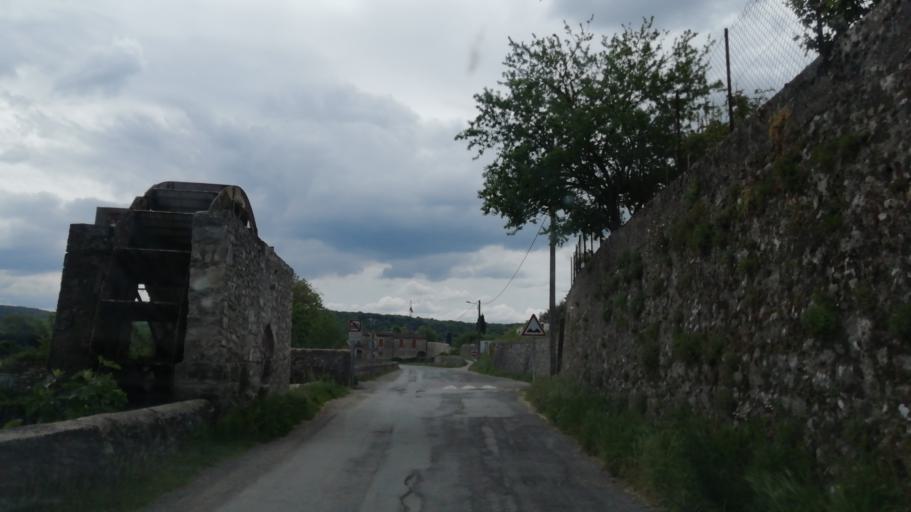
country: FR
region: Languedoc-Roussillon
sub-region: Departement de l'Herault
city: Ganges
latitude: 43.9284
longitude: 3.7037
